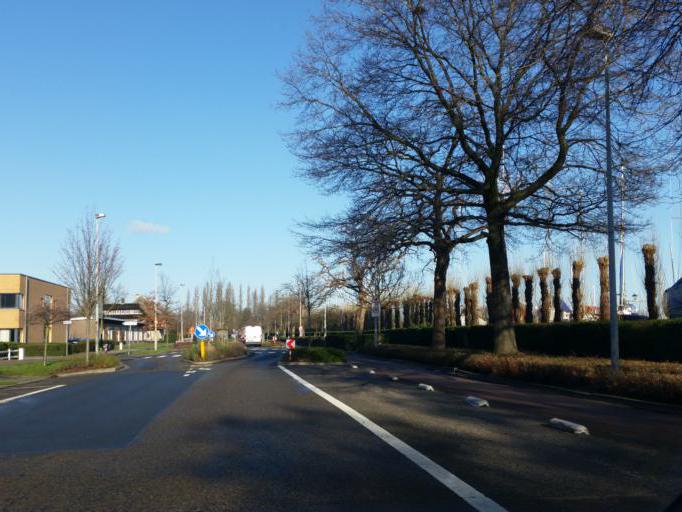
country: BE
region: Flanders
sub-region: Provincie Antwerpen
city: Antwerpen
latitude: 51.2297
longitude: 4.3917
